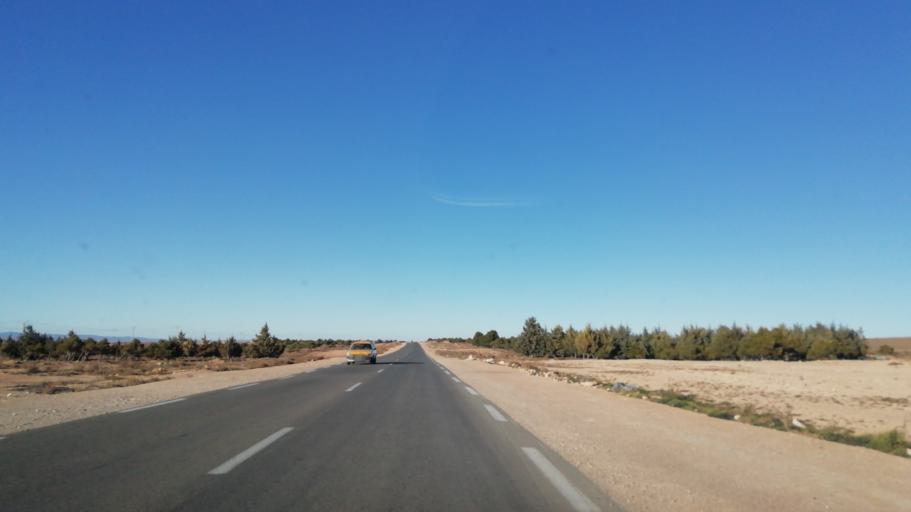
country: DZ
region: Tlemcen
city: Sebdou
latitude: 34.2684
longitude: -1.2583
